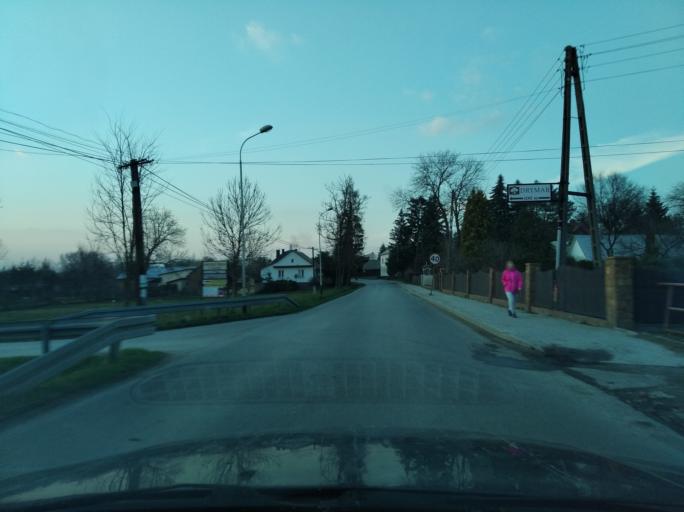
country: PL
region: Subcarpathian Voivodeship
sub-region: Powiat przeworski
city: Przeworsk
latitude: 50.0469
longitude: 22.5025
